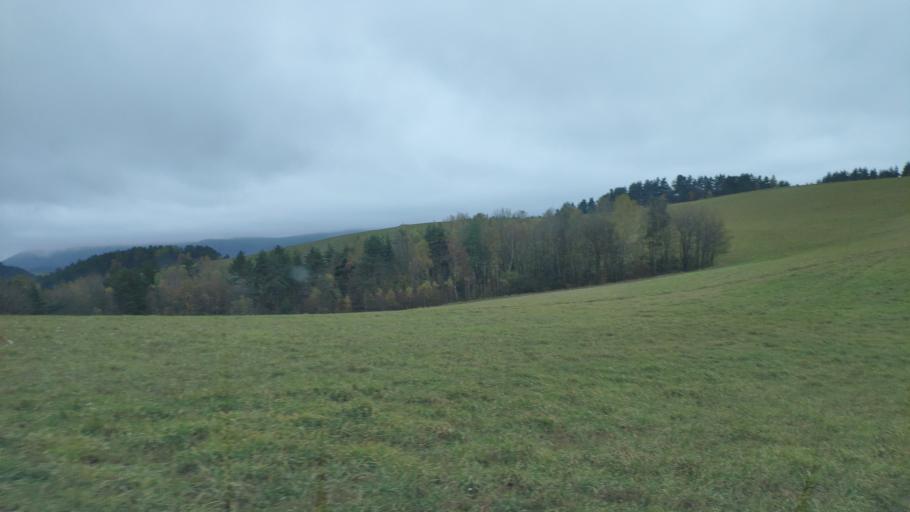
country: SK
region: Presovsky
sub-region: Okres Presov
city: Presov
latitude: 48.9350
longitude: 21.1149
